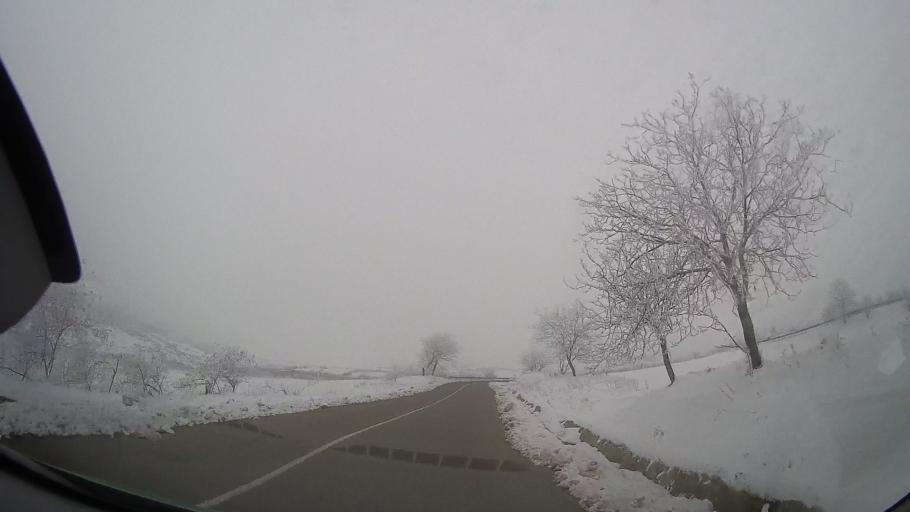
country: RO
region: Neamt
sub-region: Comuna Valea Ursului
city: Valea Ursului
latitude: 46.8053
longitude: 27.0915
